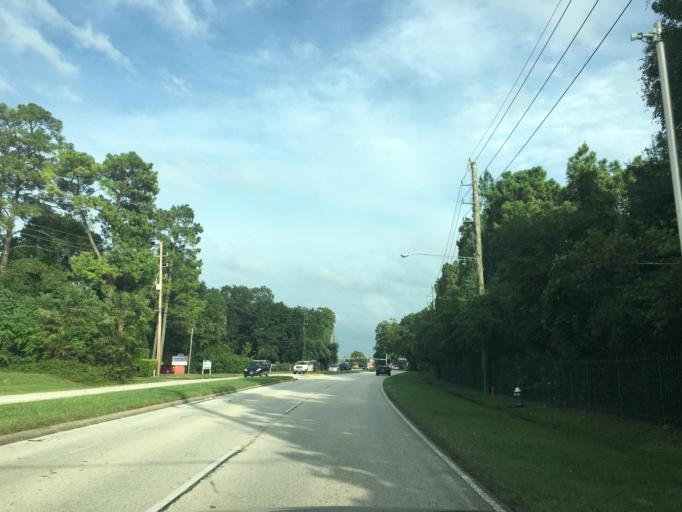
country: US
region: Texas
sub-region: Montgomery County
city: Oak Ridge North
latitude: 30.1268
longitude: -95.4610
